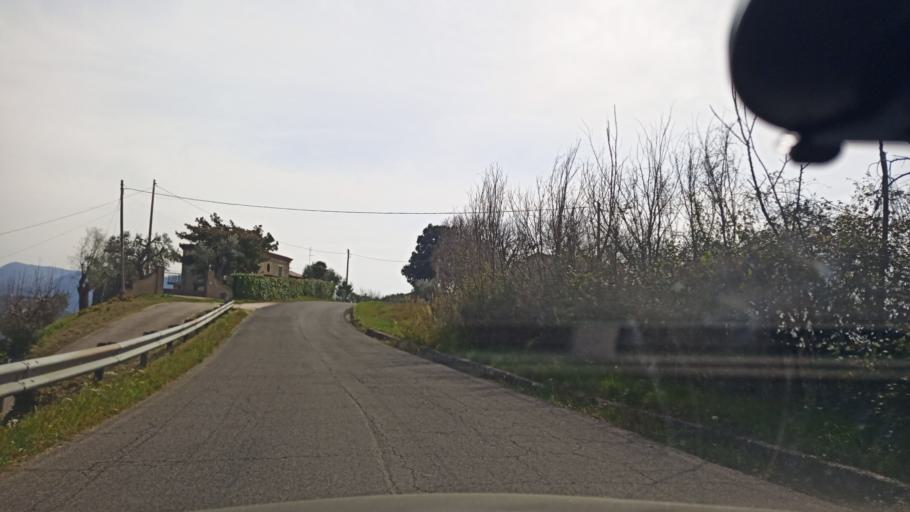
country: IT
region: Latium
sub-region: Provincia di Rieti
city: Torri in Sabina
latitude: 42.3463
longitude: 12.6502
